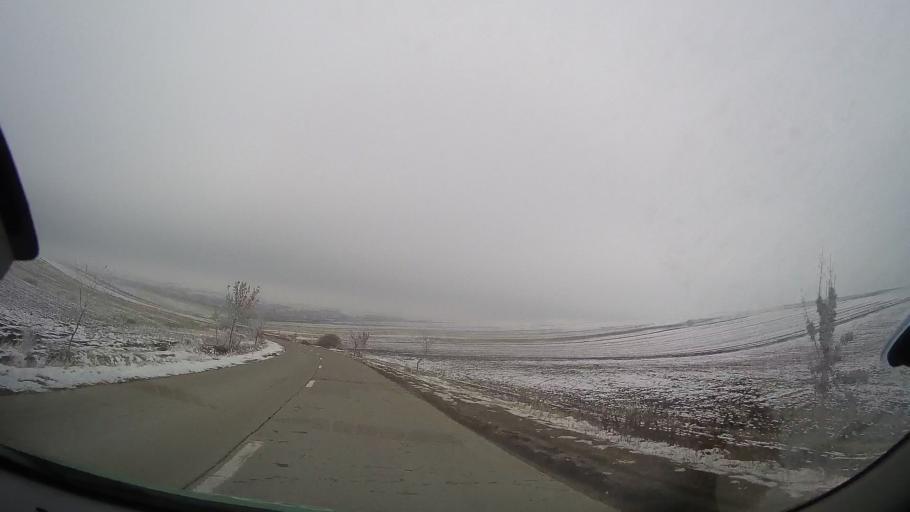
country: RO
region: Vaslui
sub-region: Comuna Ivesti
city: Ivesti
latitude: 46.2008
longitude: 27.5099
